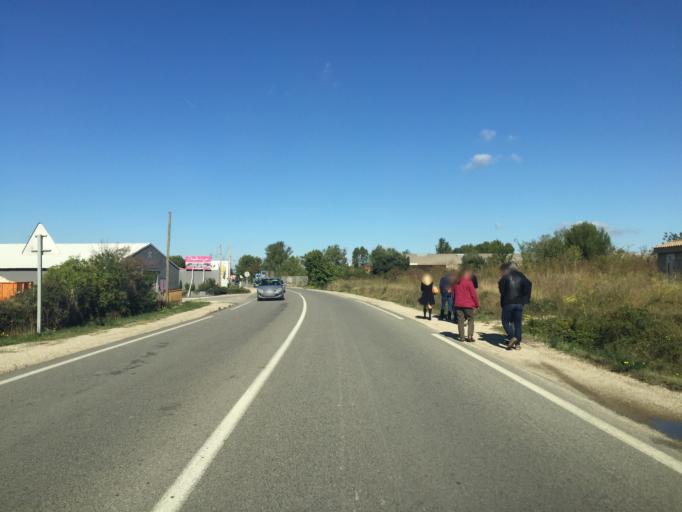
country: FR
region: Provence-Alpes-Cote d'Azur
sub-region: Departement du Vaucluse
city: Morieres-les-Avignon
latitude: 43.9554
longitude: 4.9017
